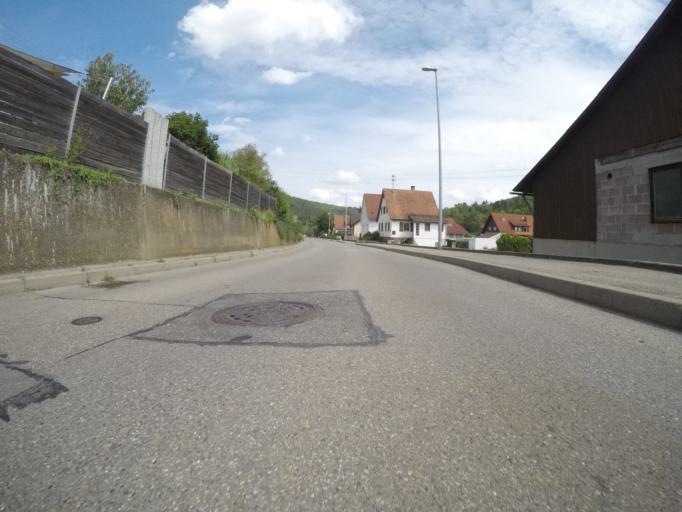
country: DE
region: Baden-Wuerttemberg
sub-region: Karlsruhe Region
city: Horb am Neckar
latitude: 48.4518
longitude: 8.7384
